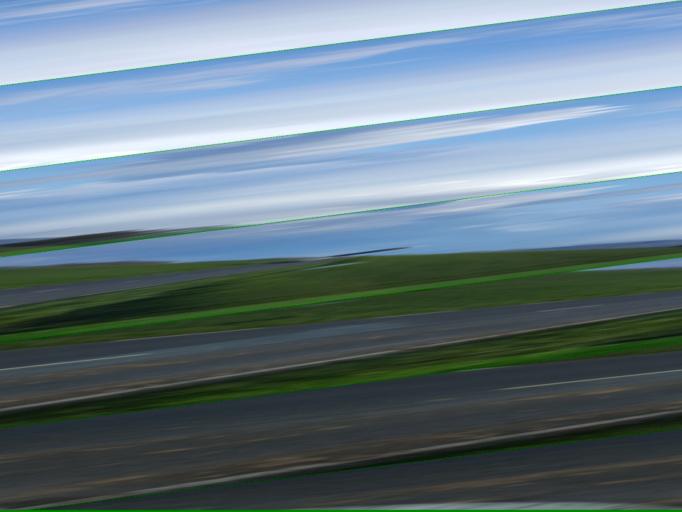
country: FR
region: Picardie
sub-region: Departement de l'Oise
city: Chaumont-en-Vexin
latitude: 49.2483
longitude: 1.8757
